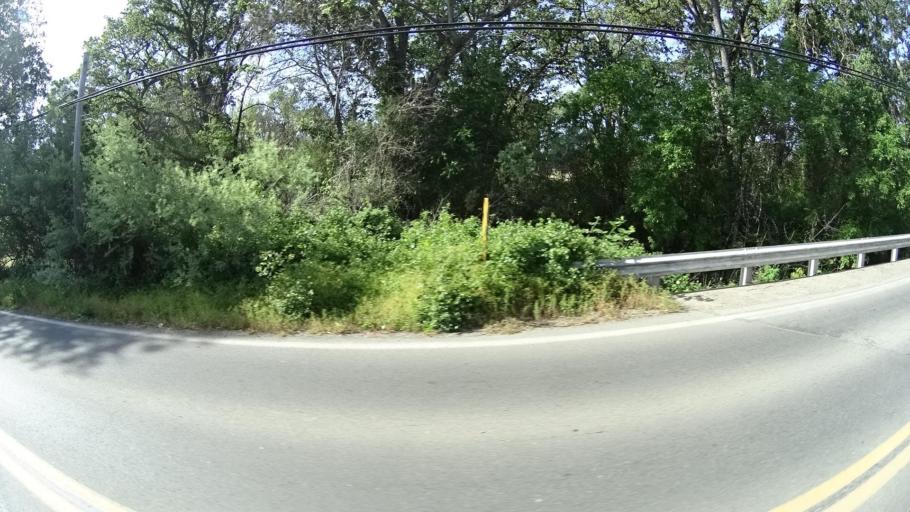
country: US
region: California
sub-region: Lake County
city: Lakeport
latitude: 39.0113
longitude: -122.9000
